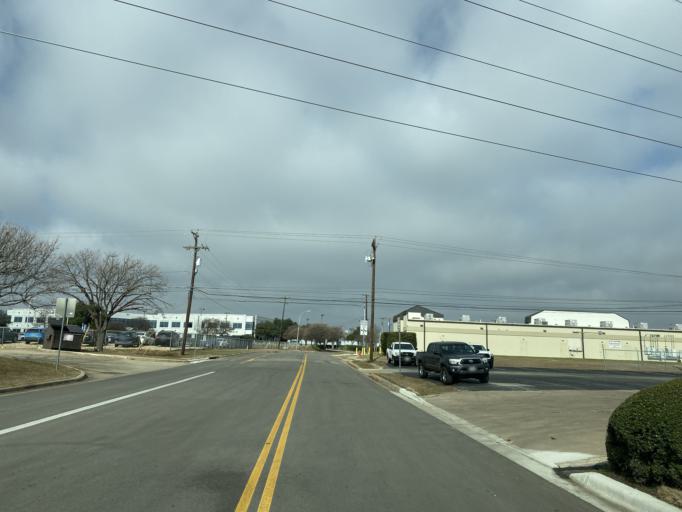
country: US
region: Texas
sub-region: Williamson County
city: Round Rock
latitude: 30.5316
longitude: -97.6874
